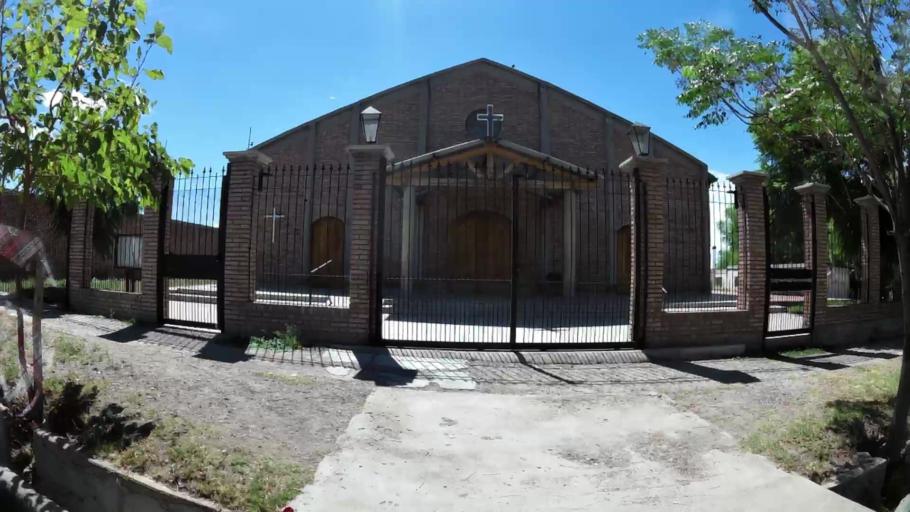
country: AR
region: Mendoza
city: Las Heras
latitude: -32.8569
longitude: -68.8641
